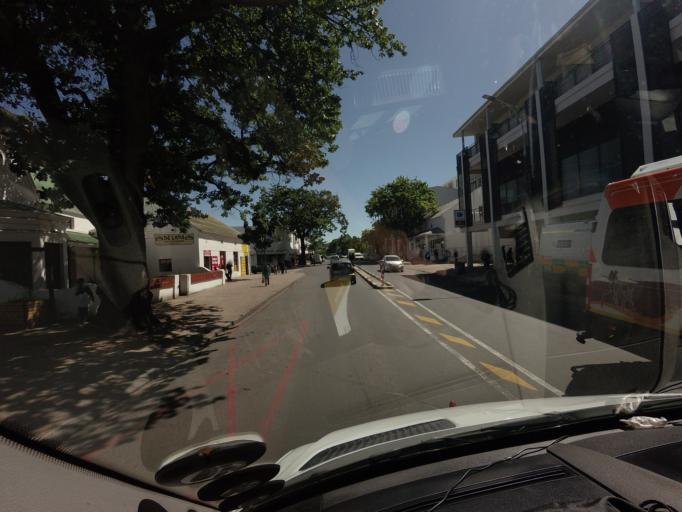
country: ZA
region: Western Cape
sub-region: Cape Winelands District Municipality
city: Stellenbosch
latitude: -33.9350
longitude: 18.8592
